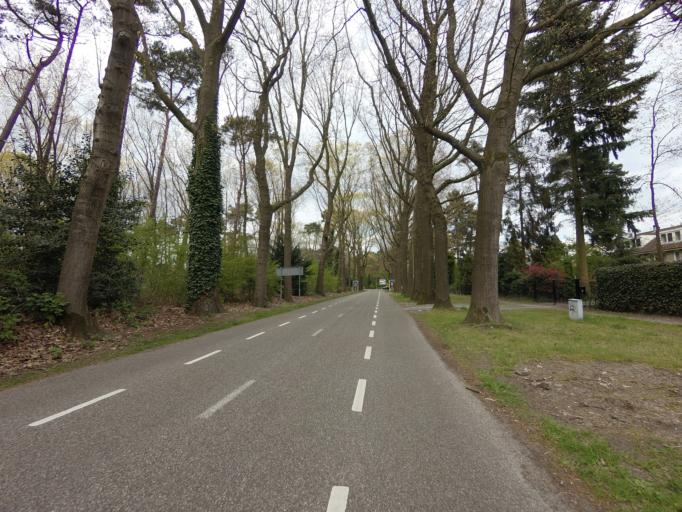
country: NL
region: Utrecht
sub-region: Gemeente Zeist
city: Zeist
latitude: 52.1349
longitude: 5.2334
